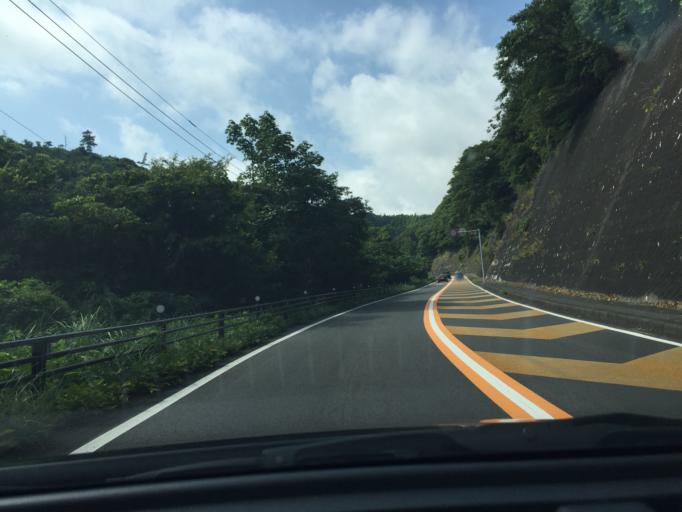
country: JP
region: Shizuoka
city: Ito
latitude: 34.9681
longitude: 139.1240
